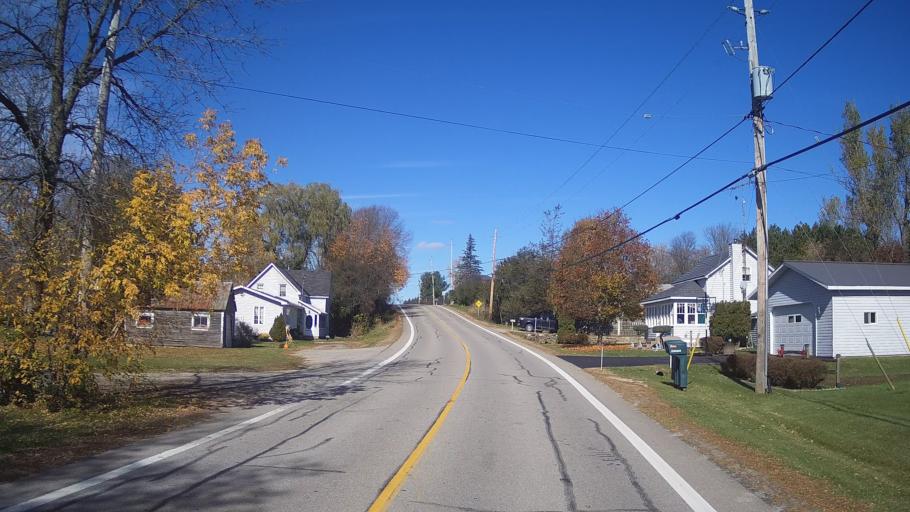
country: CA
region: Ontario
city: Perth
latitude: 44.8770
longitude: -76.3039
